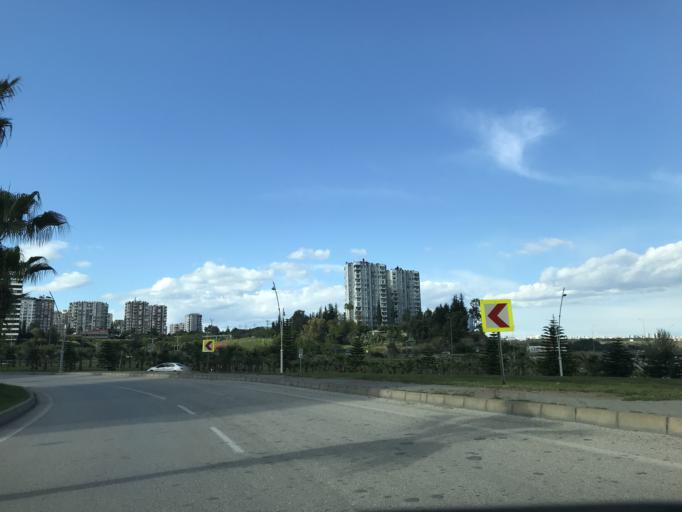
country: TR
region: Adana
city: Adana
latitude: 37.0228
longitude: 35.3207
